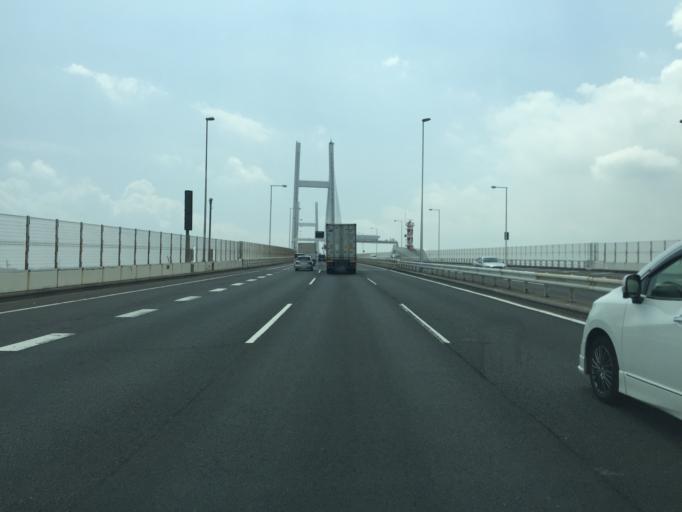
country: JP
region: Kanagawa
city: Yokohama
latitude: 35.4610
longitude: 139.6784
